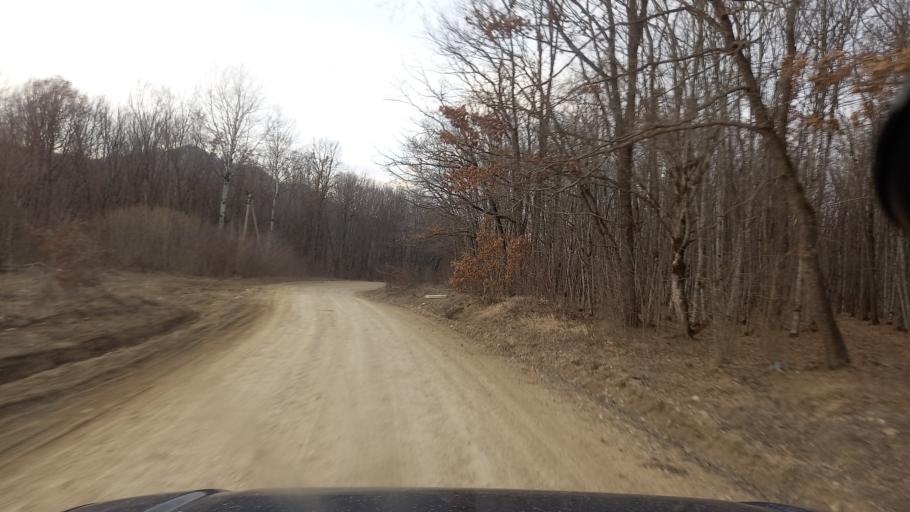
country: RU
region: Adygeya
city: Kamennomostskiy
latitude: 44.1618
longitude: 40.2450
